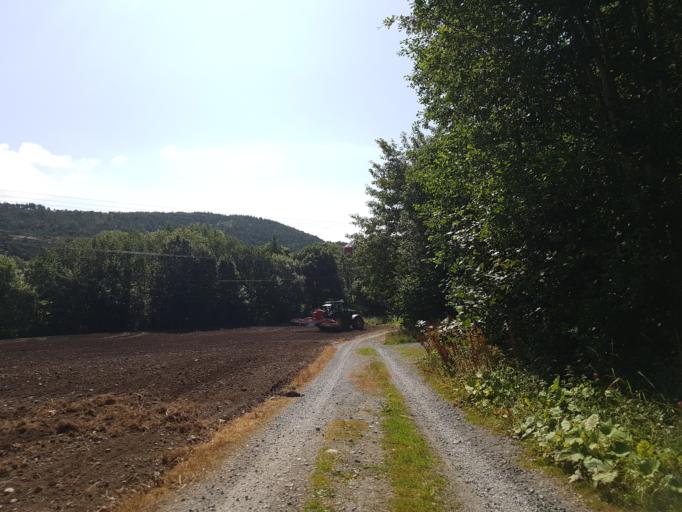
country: NO
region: Sor-Trondelag
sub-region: Agdenes
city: Lensvik
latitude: 63.6326
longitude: 9.8409
